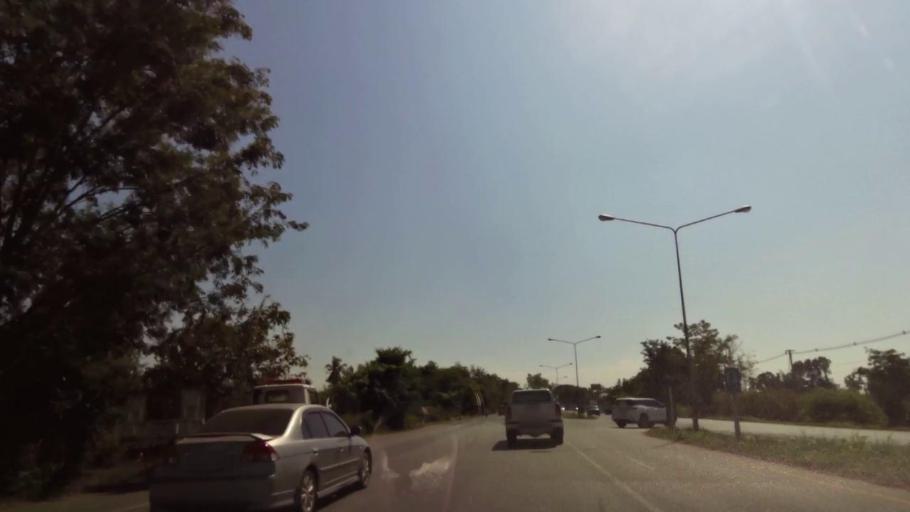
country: TH
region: Nakhon Sawan
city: Kao Liao
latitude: 15.8250
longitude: 100.1191
